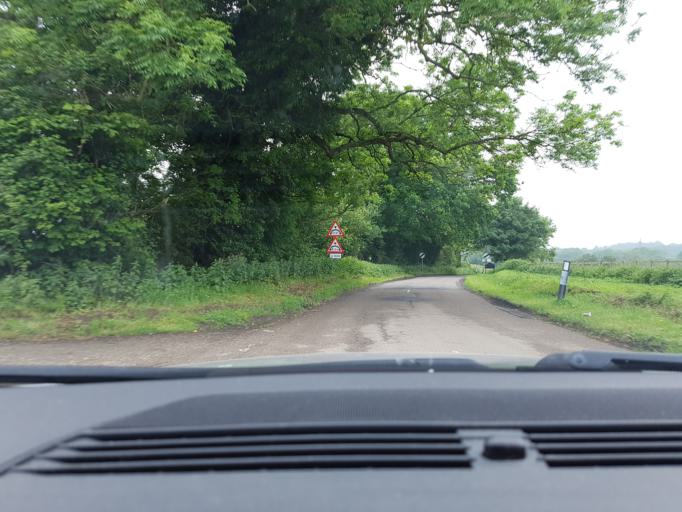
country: GB
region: England
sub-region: Buckinghamshire
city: Winslow
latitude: 51.9427
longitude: -0.8927
